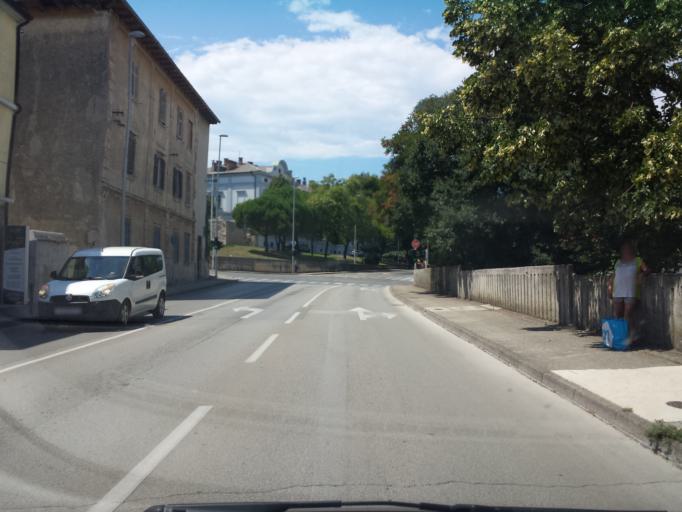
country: HR
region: Istarska
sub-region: Grad Pula
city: Pula
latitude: 44.8609
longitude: 13.8465
